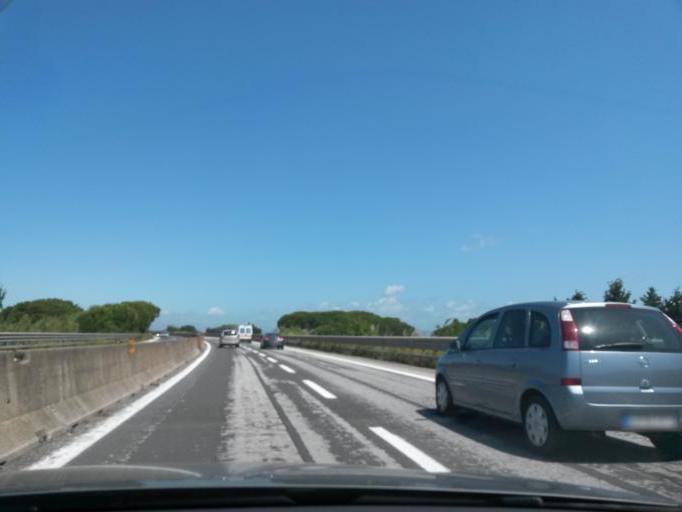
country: IT
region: Tuscany
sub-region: Provincia di Livorno
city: La California
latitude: 43.2406
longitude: 10.5560
